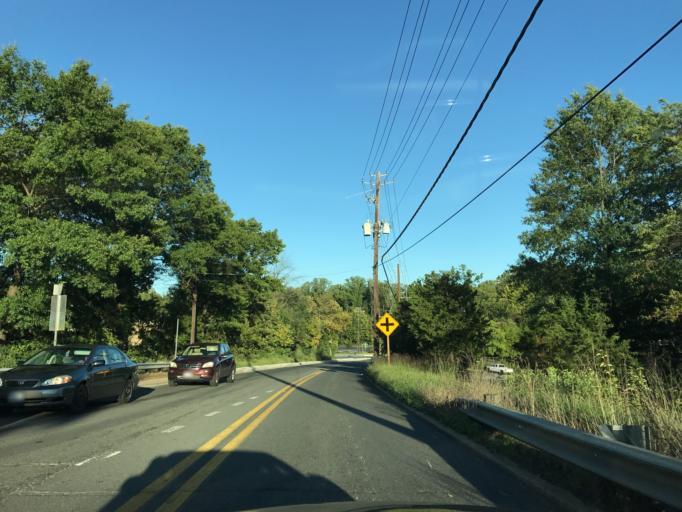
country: US
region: Maryland
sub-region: Prince George's County
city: Beltsville
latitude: 39.0345
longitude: -76.9053
